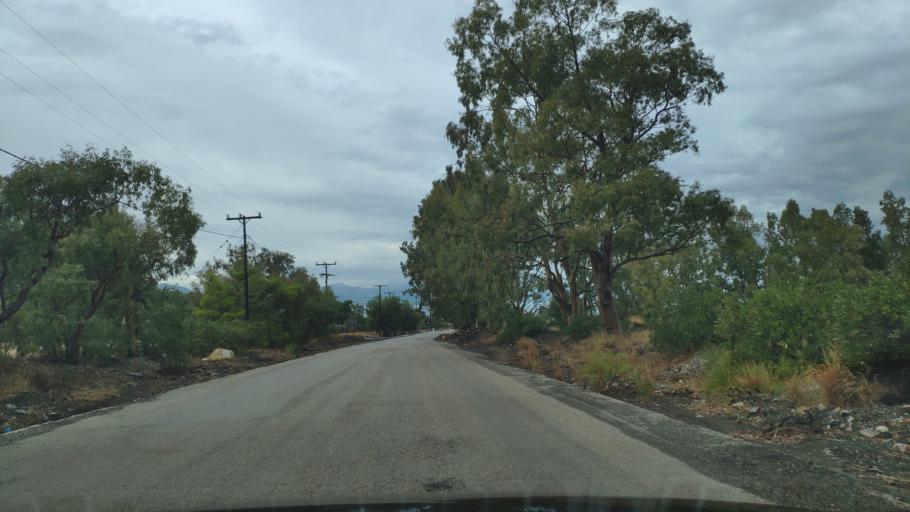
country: GR
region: Peloponnese
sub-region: Nomos Korinthias
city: Loutraki
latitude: 37.9649
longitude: 23.0036
